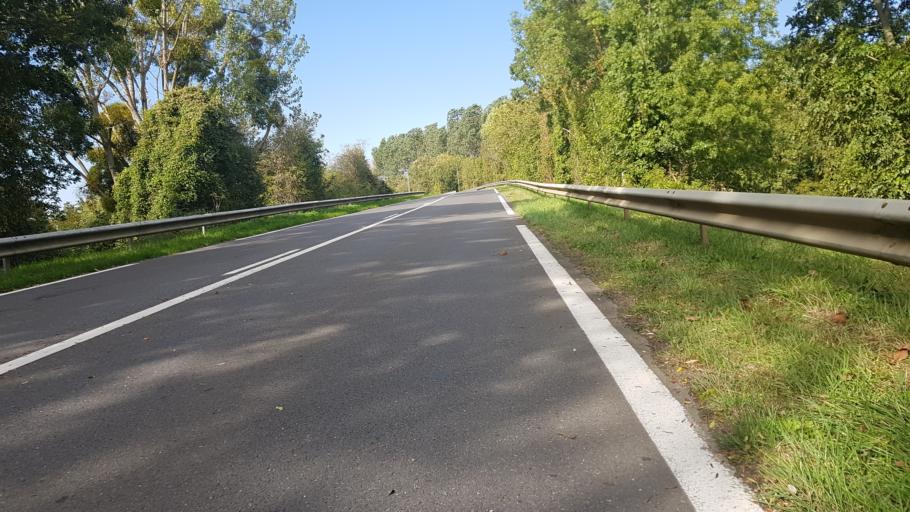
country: FR
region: Poitou-Charentes
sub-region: Departement de la Vienne
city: Chasseneuil-du-Poitou
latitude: 46.6339
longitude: 0.3620
